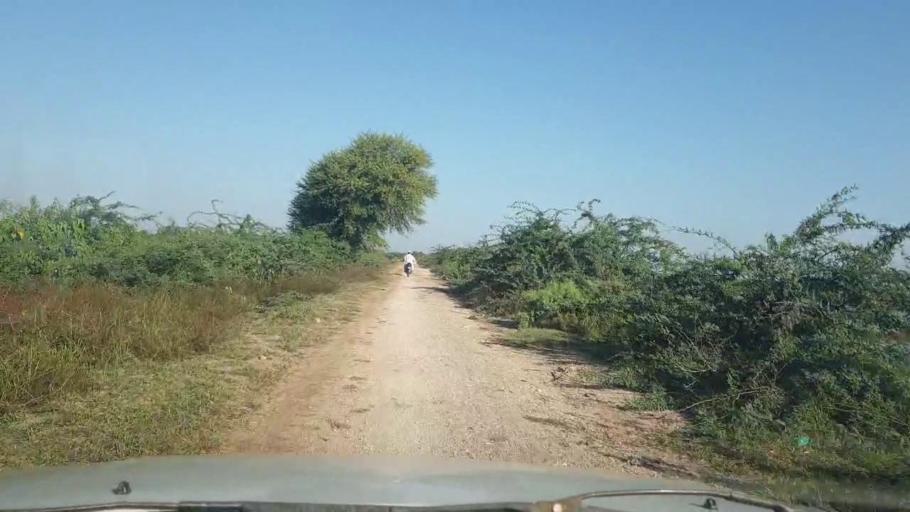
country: PK
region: Sindh
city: Chuhar Jamali
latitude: 24.5476
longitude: 67.9106
